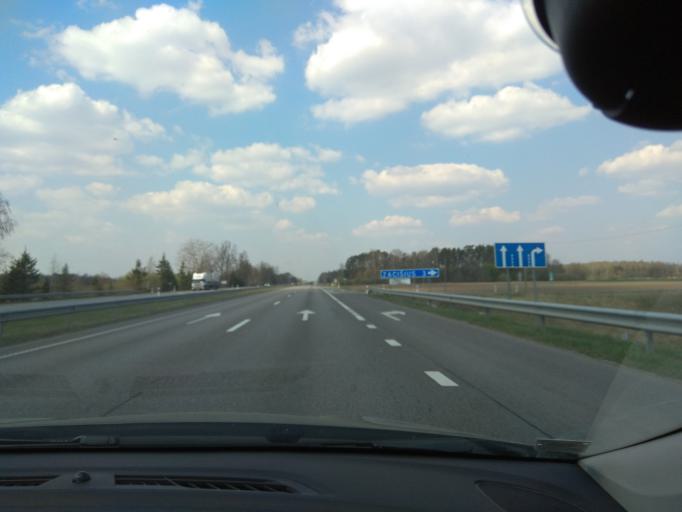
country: LT
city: Vilkija
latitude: 55.1241
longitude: 23.7502
